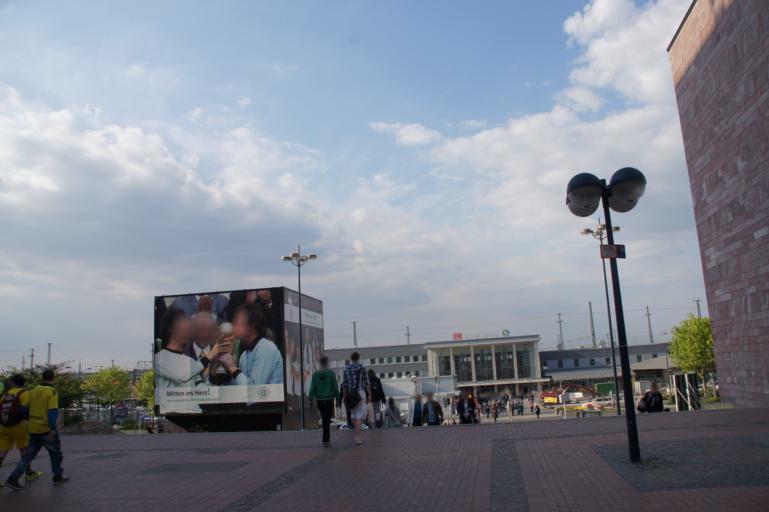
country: DE
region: North Rhine-Westphalia
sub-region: Regierungsbezirk Arnsberg
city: Dortmund
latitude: 51.5161
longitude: 7.4599
